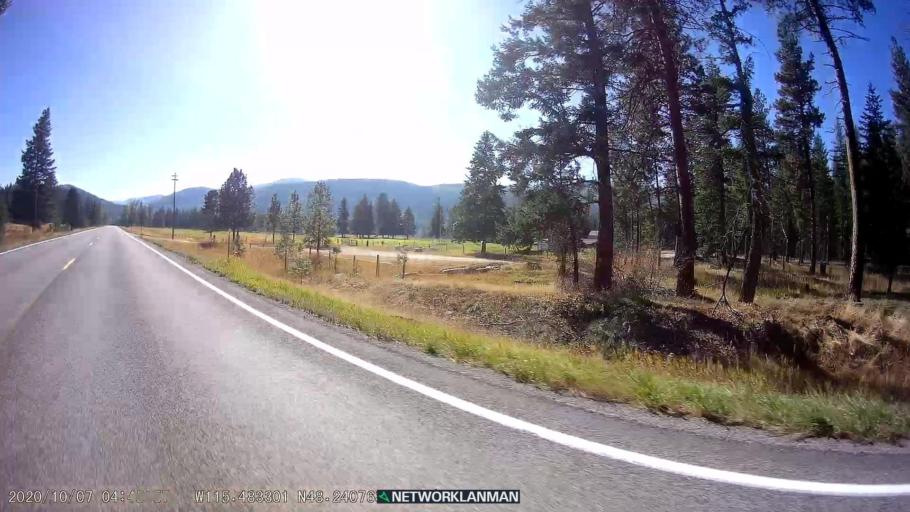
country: US
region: Montana
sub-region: Lincoln County
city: Libby
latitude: 48.2403
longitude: -115.4832
